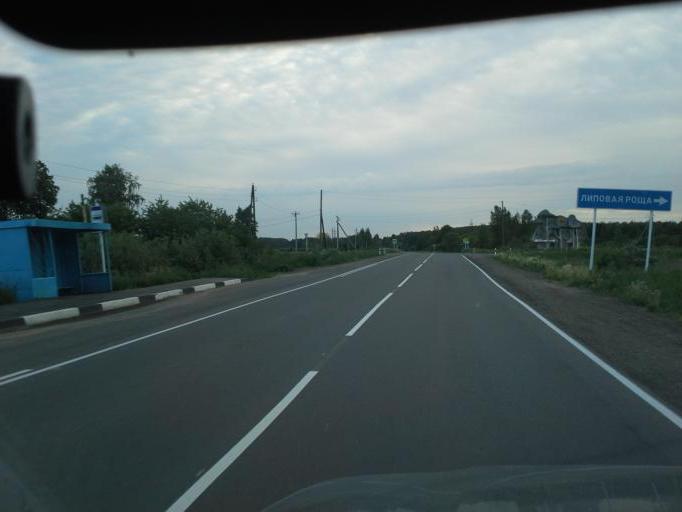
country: RU
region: Ivanovo
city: Petrovskiy
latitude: 56.6273
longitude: 40.2837
